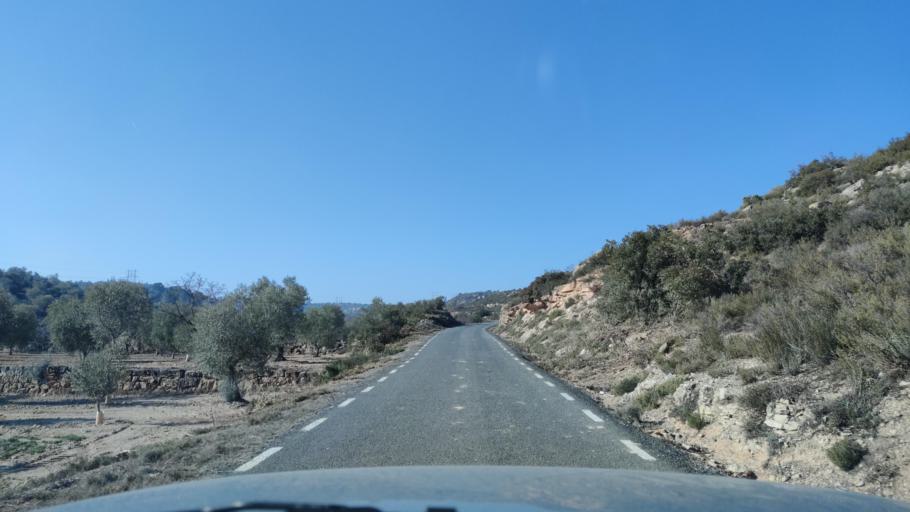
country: ES
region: Catalonia
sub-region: Provincia de Lleida
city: Torrebesses
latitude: 41.4324
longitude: 0.5779
